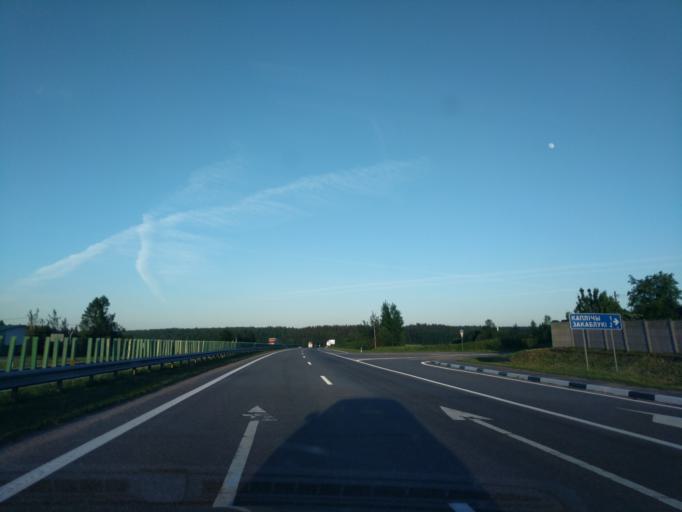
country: BY
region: Minsk
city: Novosel'ye
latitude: 53.9136
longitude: 27.2408
